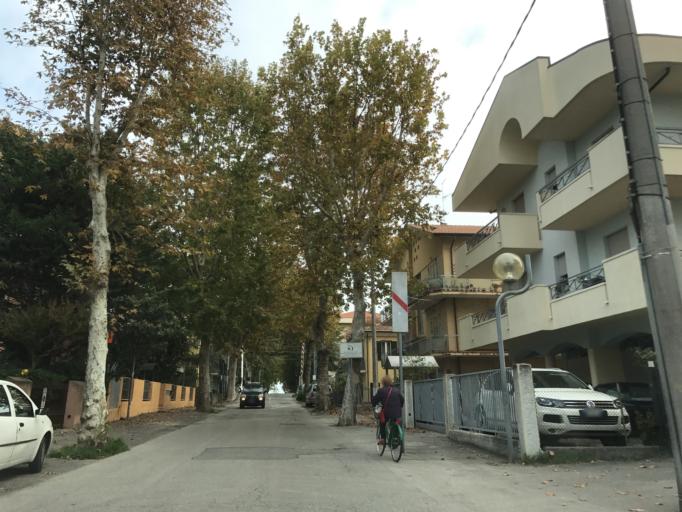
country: IT
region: Emilia-Romagna
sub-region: Provincia di Rimini
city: Rimini
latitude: 44.0820
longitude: 12.5413
